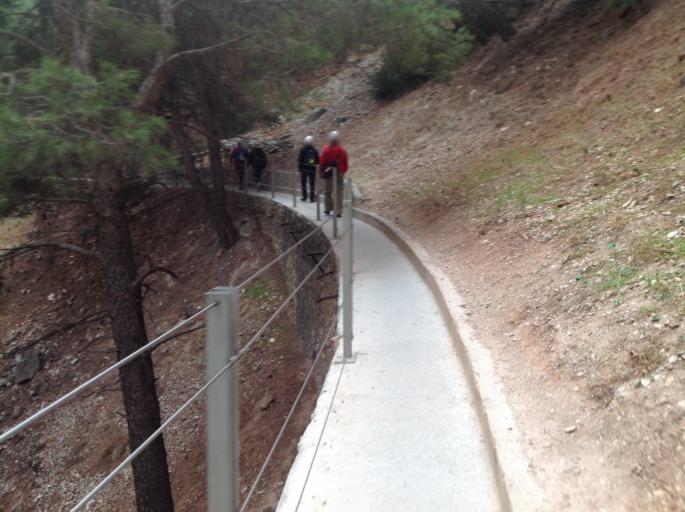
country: ES
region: Andalusia
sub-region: Provincia de Malaga
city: Ardales
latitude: 36.9288
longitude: -4.7838
